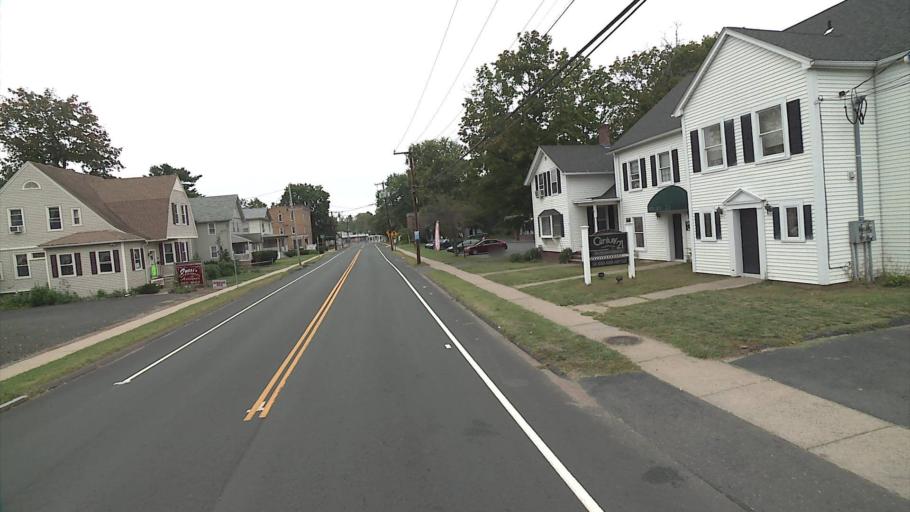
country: US
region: Connecticut
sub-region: Hartford County
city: Windsor
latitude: 41.8544
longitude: -72.6470
